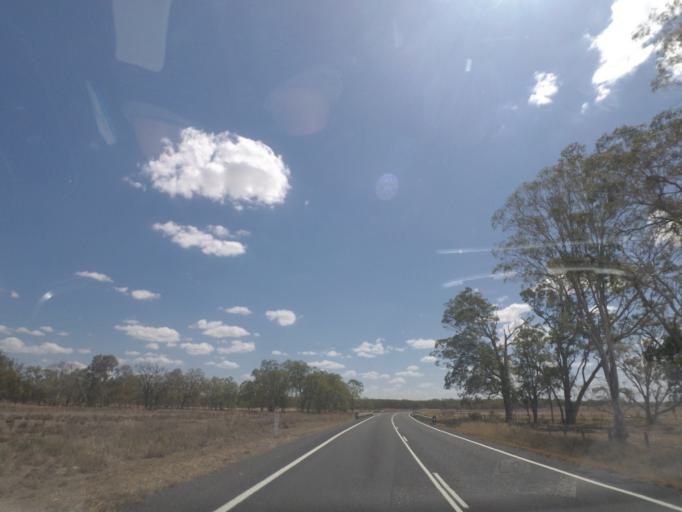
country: AU
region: Queensland
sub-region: Southern Downs
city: Warwick
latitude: -28.1828
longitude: 151.8177
